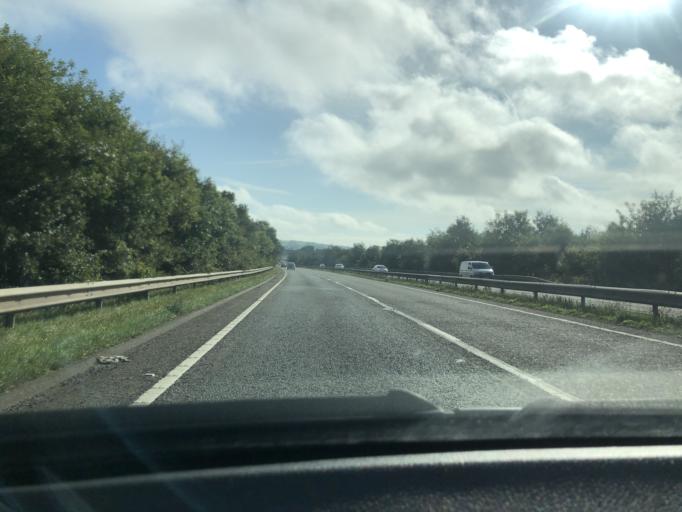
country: GB
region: England
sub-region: Devon
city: Crediton
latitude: 50.7271
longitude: -3.7067
